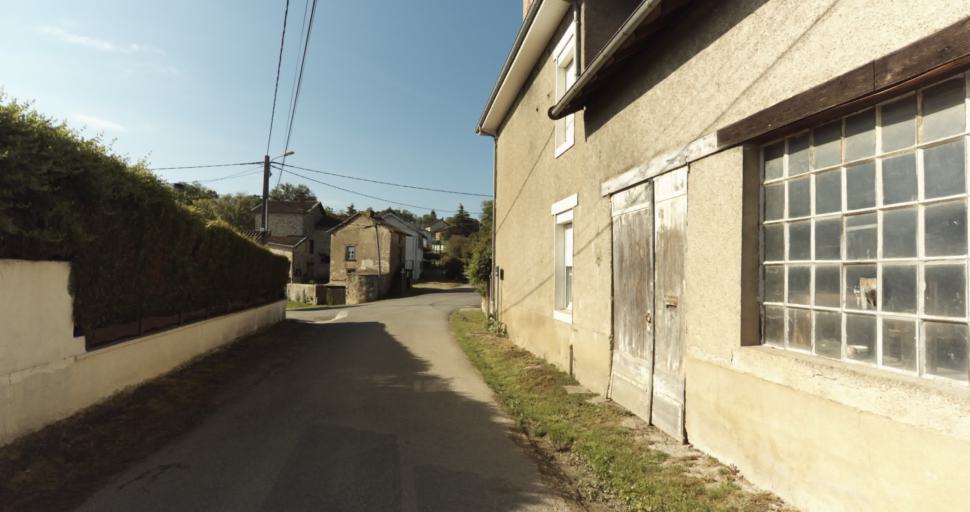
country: FR
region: Limousin
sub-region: Departement de la Haute-Vienne
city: Solignac
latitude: 45.7292
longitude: 1.2446
